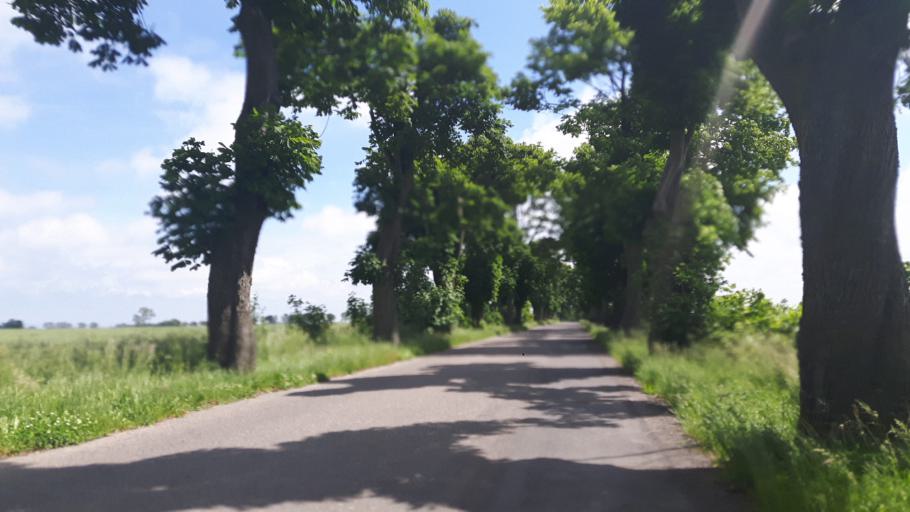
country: PL
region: West Pomeranian Voivodeship
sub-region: Powiat slawienski
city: Slawno
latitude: 54.5086
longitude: 16.5889
